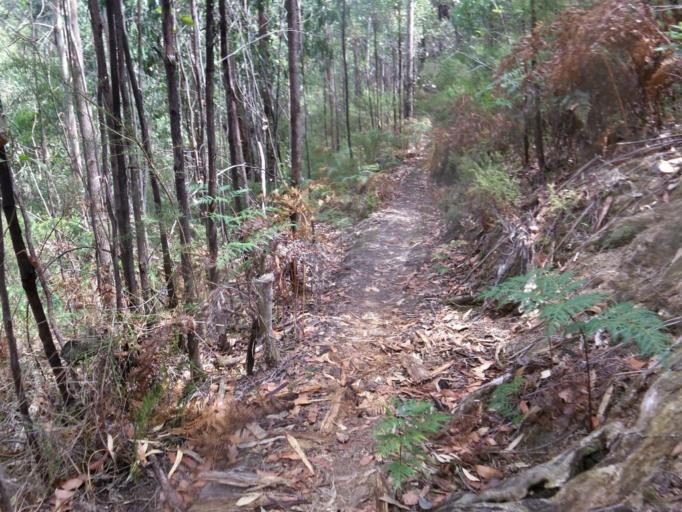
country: AU
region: Victoria
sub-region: Nillumbik
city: Saint Andrews
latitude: -37.5475
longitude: 145.3463
